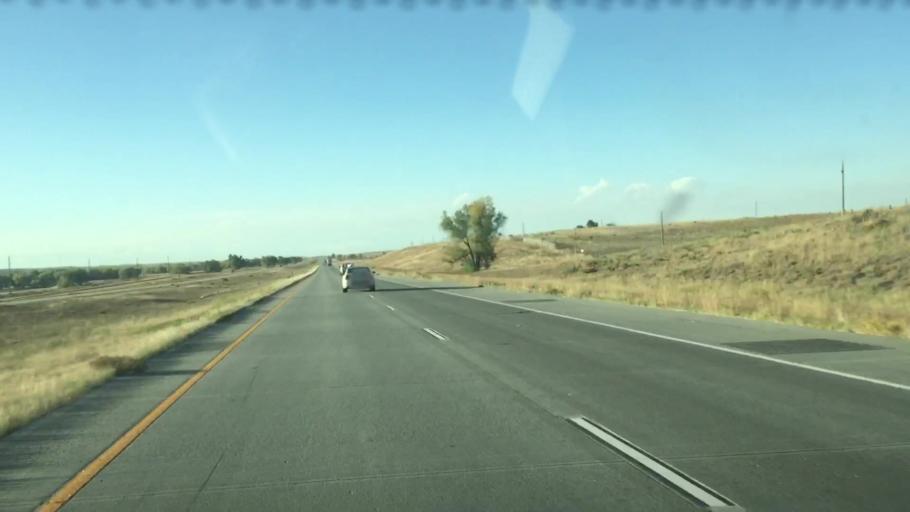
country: US
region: Colorado
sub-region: Arapahoe County
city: Byers
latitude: 39.5514
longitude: -104.0038
